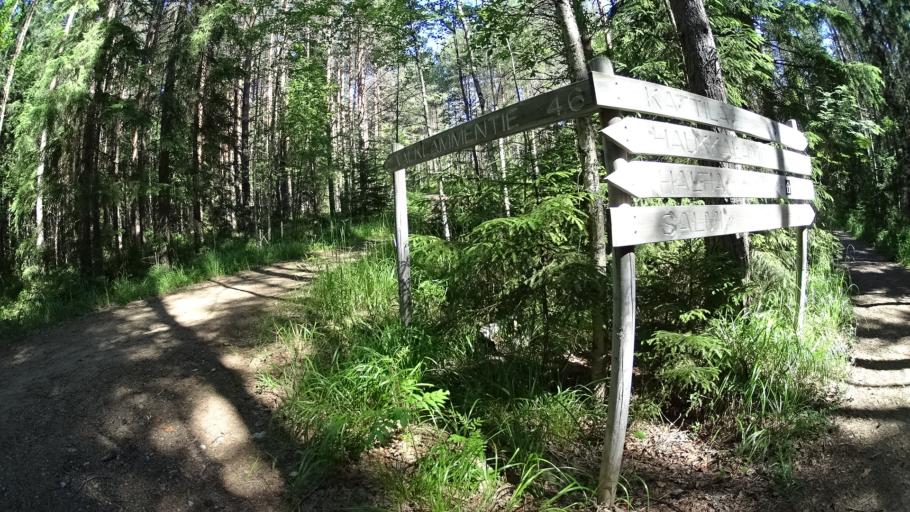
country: FI
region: Uusimaa
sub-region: Helsinki
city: Vihti
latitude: 60.3236
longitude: 24.4925
